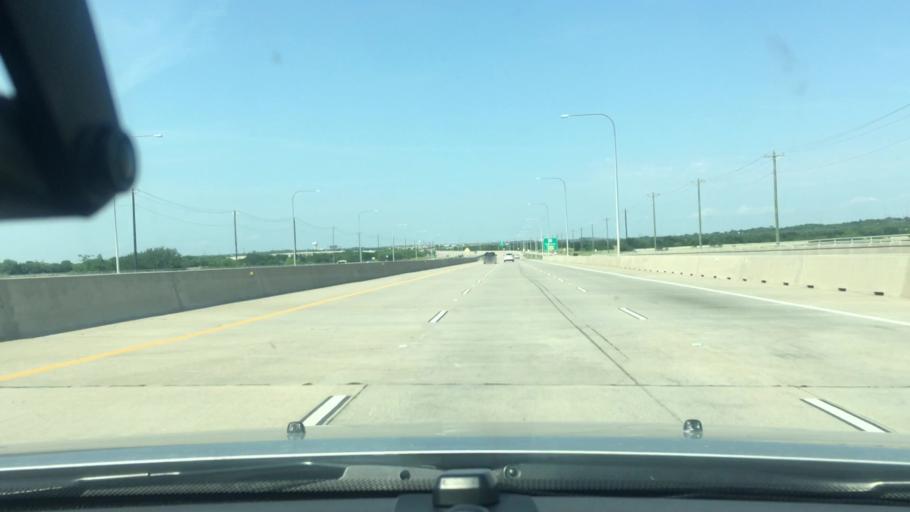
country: US
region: Texas
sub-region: Collin County
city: Prosper
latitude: 33.1990
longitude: -96.8304
